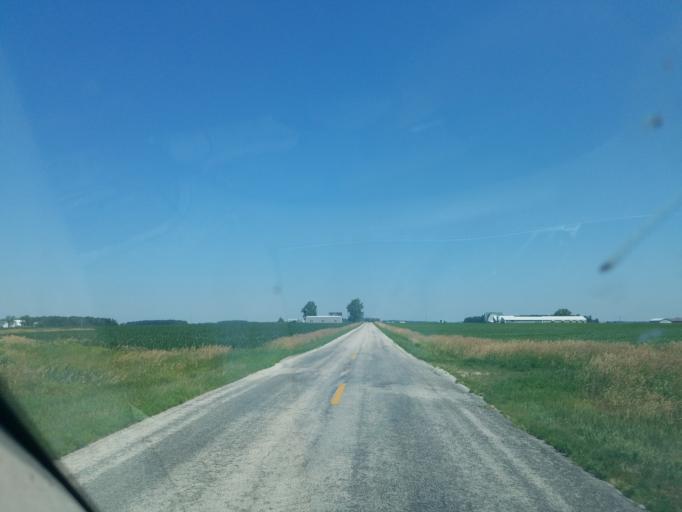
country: US
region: Ohio
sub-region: Mercer County
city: Rockford
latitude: 40.6284
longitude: -84.7086
